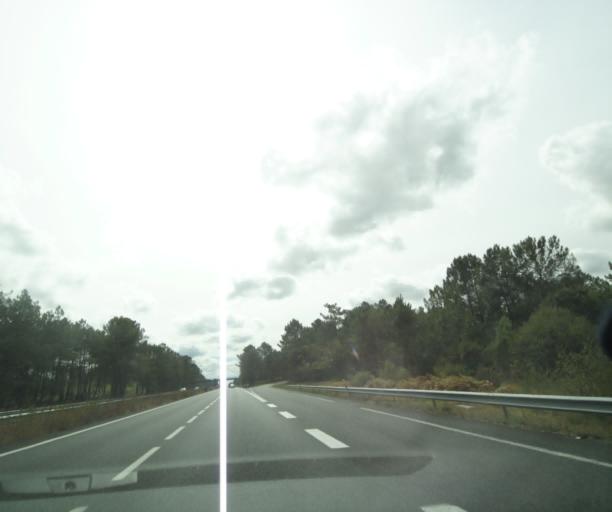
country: FR
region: Aquitaine
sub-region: Departement de la Gironde
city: Marcillac
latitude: 45.2575
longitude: -0.5445
